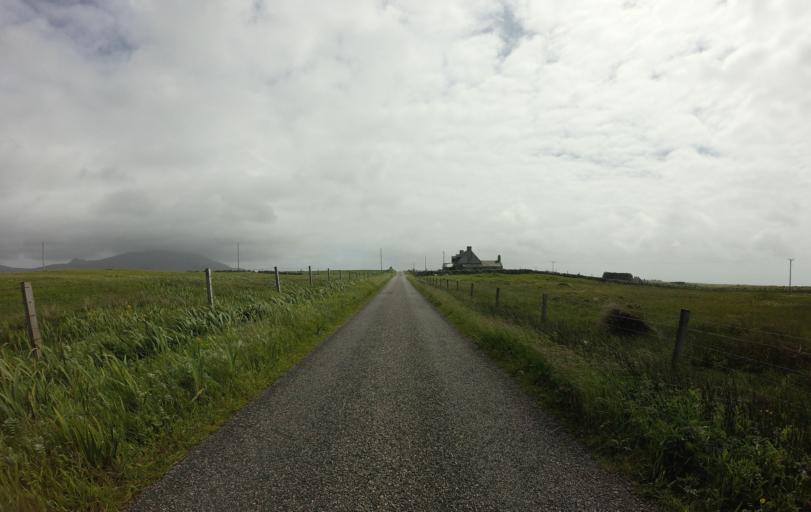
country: GB
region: Scotland
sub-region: Eilean Siar
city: Isle of South Uist
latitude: 57.2754
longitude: -7.4092
